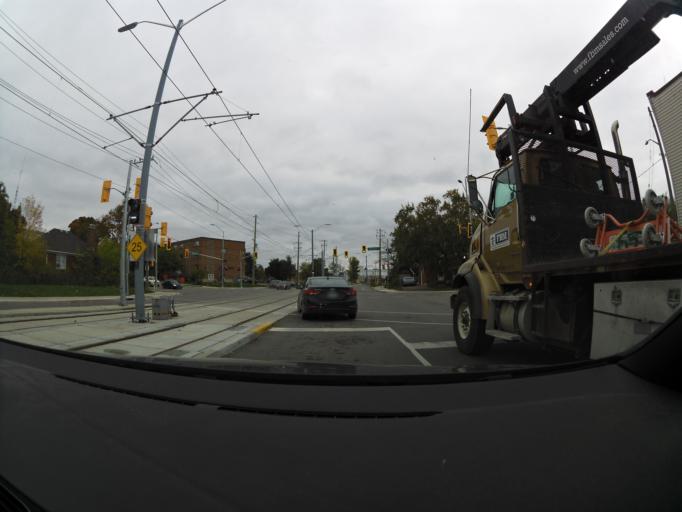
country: CA
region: Ontario
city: Kitchener
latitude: 43.4441
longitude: -80.4793
